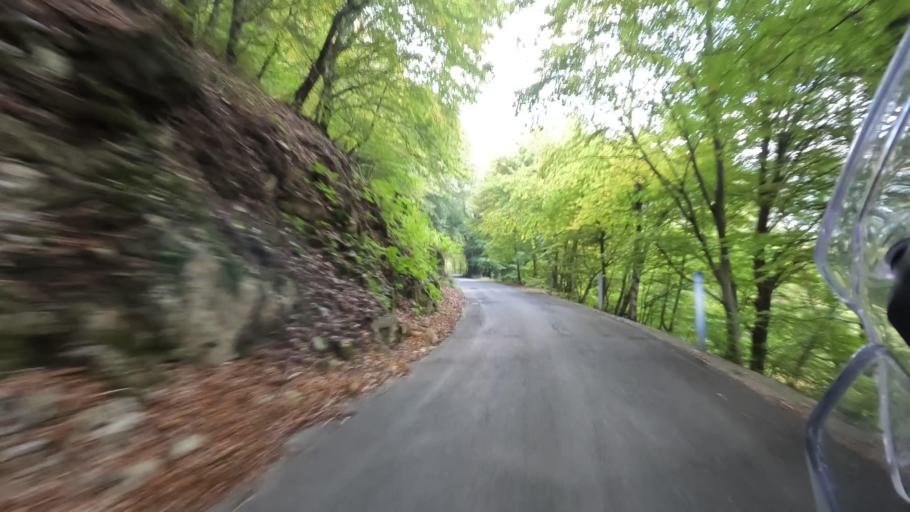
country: IT
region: Lombardy
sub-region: Provincia di Como
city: Pigra
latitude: 45.9640
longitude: 9.1231
